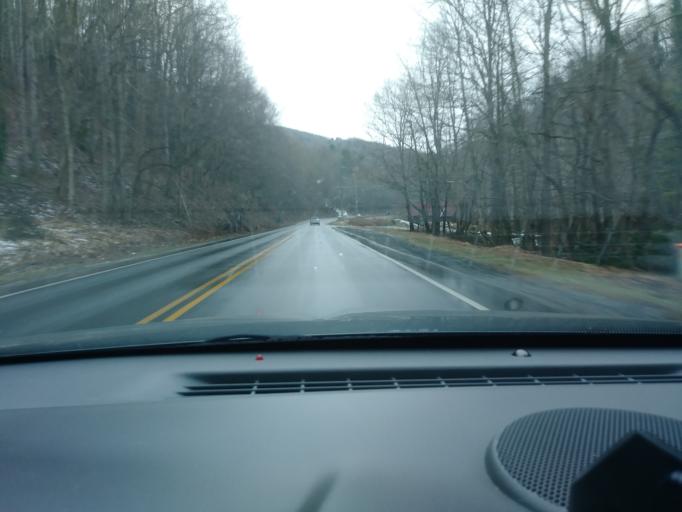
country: US
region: North Carolina
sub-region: Watauga County
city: Foscoe
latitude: 36.1987
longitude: -81.7387
